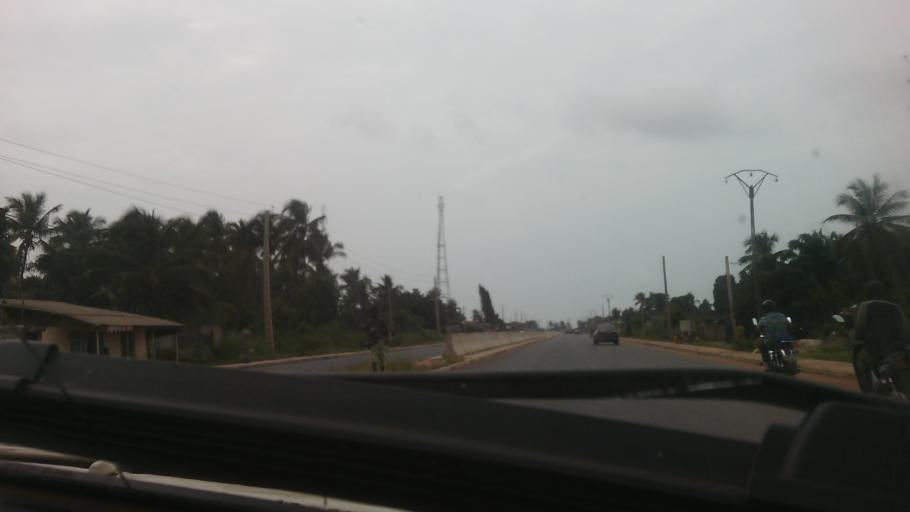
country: BJ
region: Atlantique
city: Ouidah
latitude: 6.3689
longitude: 2.0951
